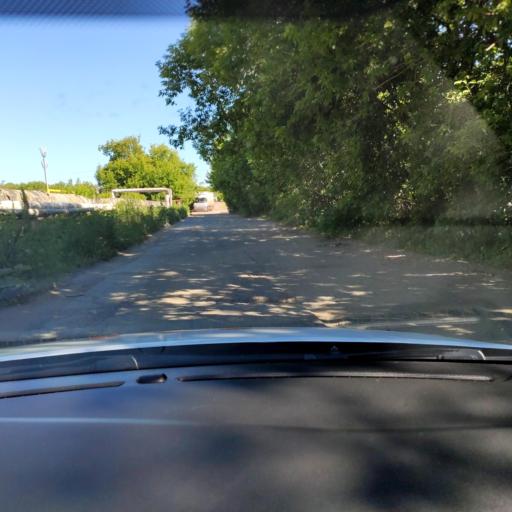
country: RU
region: Tatarstan
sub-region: Gorod Kazan'
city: Kazan
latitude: 55.8471
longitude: 49.0549
